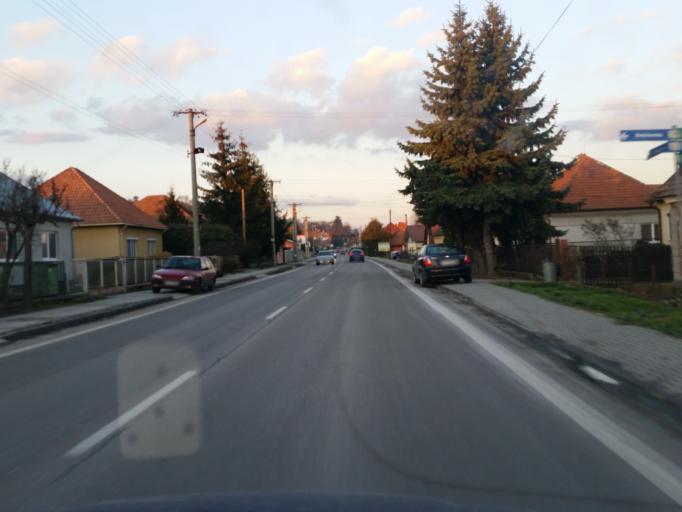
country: SK
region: Nitriansky
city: Banovce nad Bebravou
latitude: 48.5873
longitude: 18.2004
